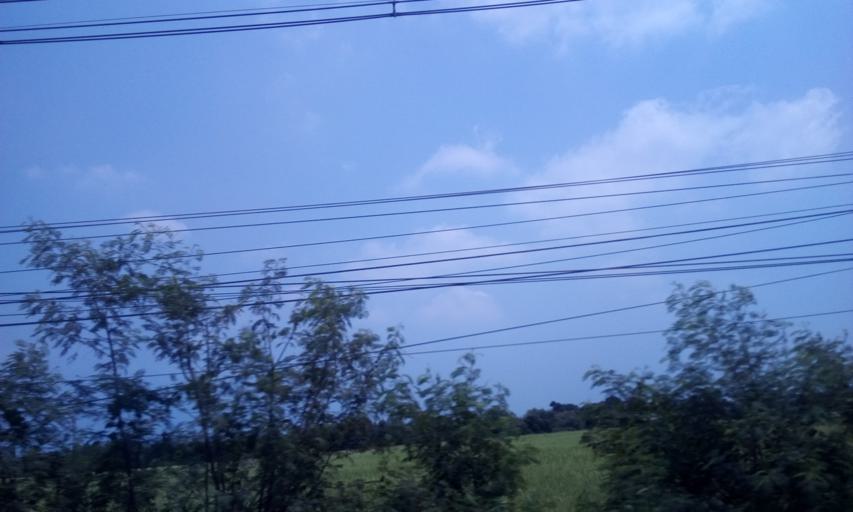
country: TH
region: Chachoengsao
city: Chachoengsao
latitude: 13.7299
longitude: 101.0884
